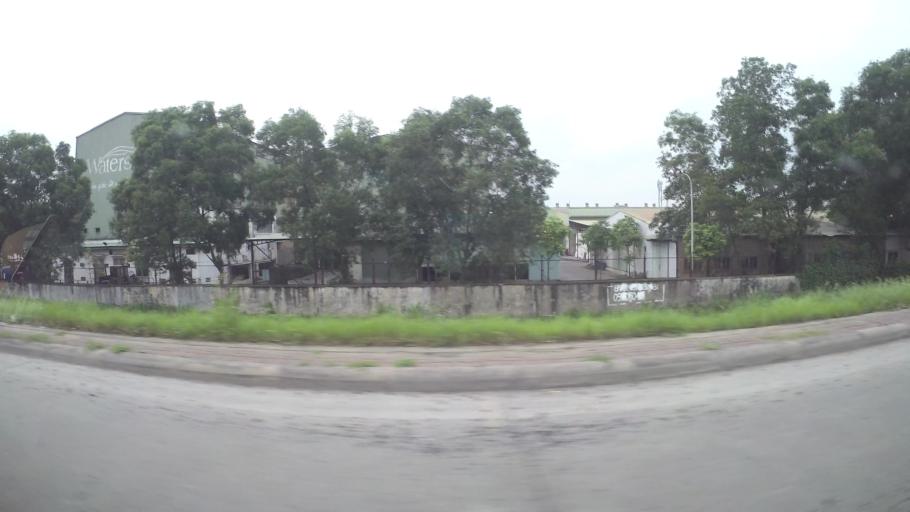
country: VN
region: Ha Noi
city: Trau Quy
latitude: 21.0762
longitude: 105.9100
